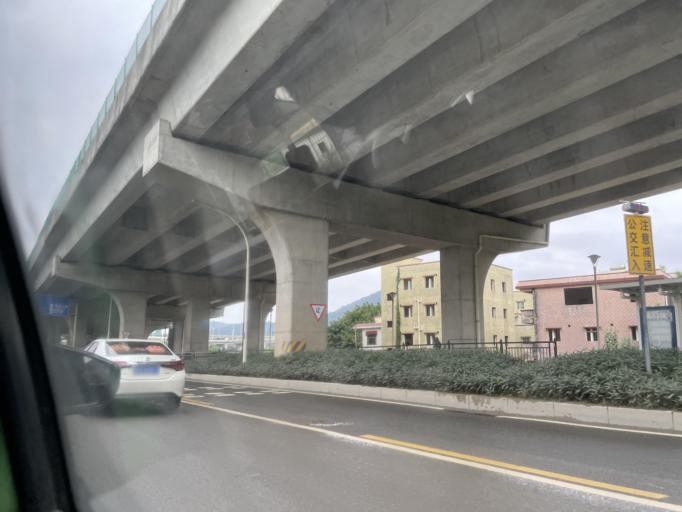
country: CN
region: Guangdong
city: Nanping
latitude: 22.1764
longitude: 113.4682
